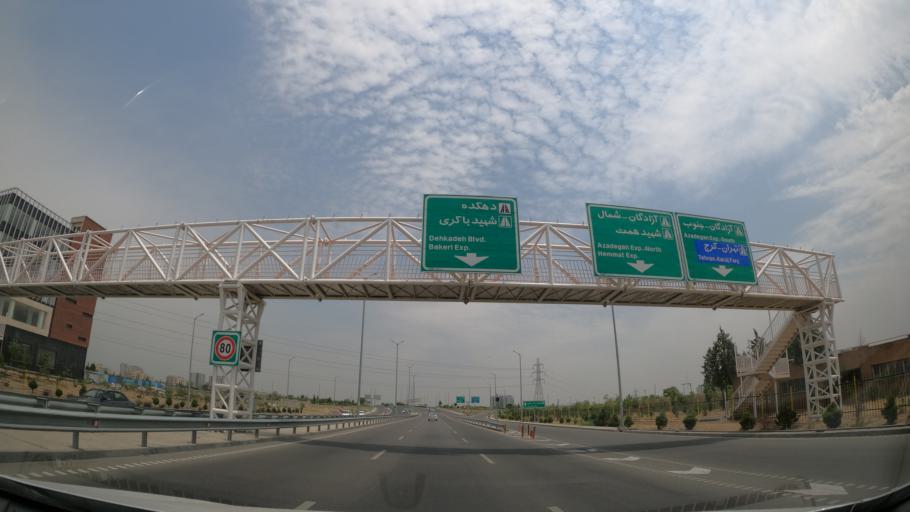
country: IR
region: Tehran
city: Shahr-e Qods
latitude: 35.7403
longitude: 51.2489
